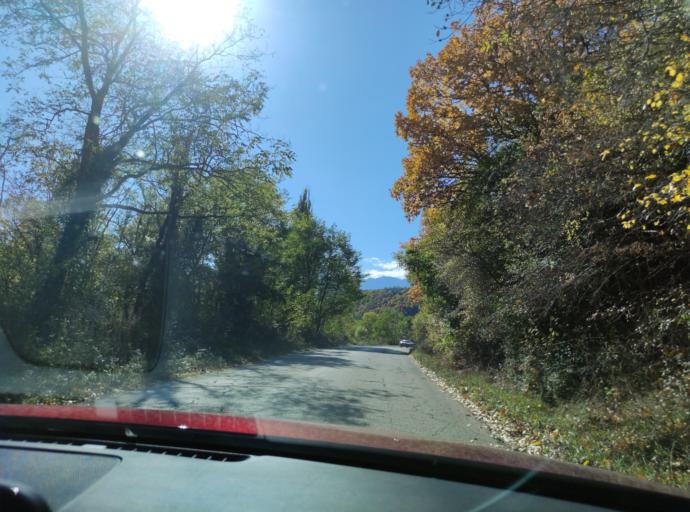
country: BG
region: Montana
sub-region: Obshtina Chiprovtsi
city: Chiprovtsi
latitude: 43.3977
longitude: 22.9264
